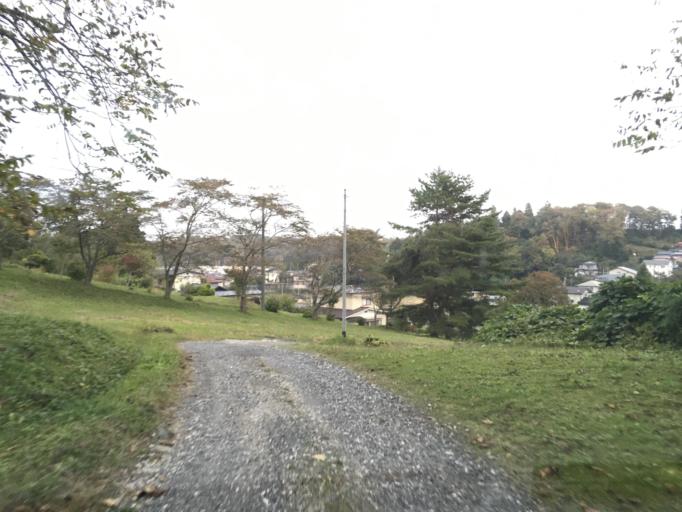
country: JP
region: Iwate
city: Ichinoseki
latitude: 38.9147
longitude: 141.1249
